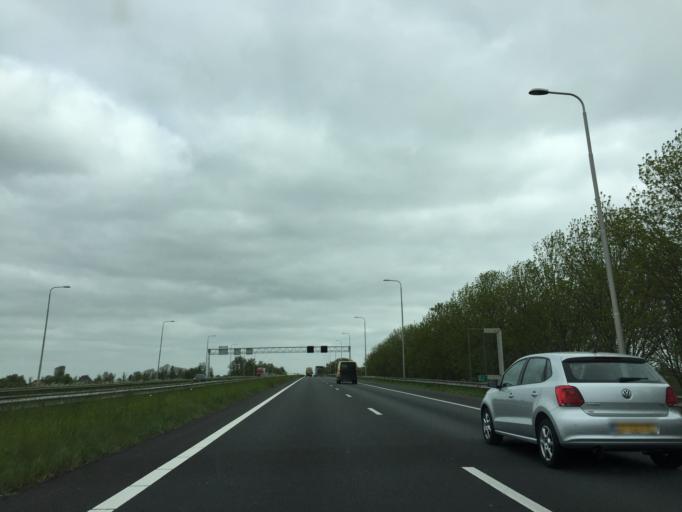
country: NL
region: North Holland
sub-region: Gemeente Beemster
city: Halfweg
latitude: 52.5833
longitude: 4.9805
